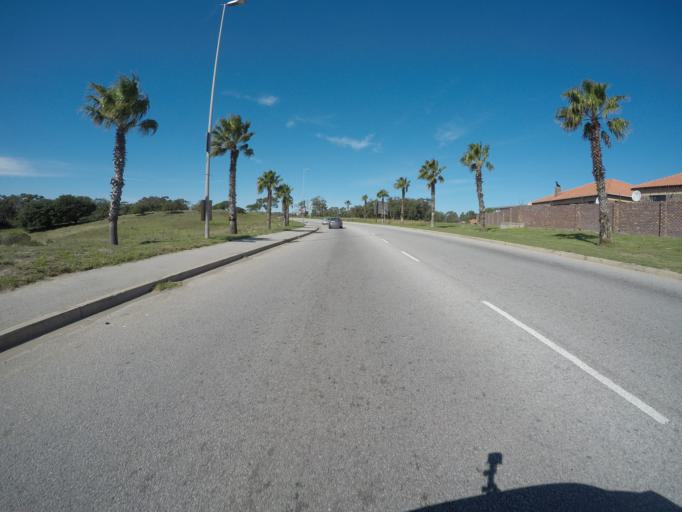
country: ZA
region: Eastern Cape
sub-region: Nelson Mandela Bay Metropolitan Municipality
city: Port Elizabeth
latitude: -33.9816
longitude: 25.6358
